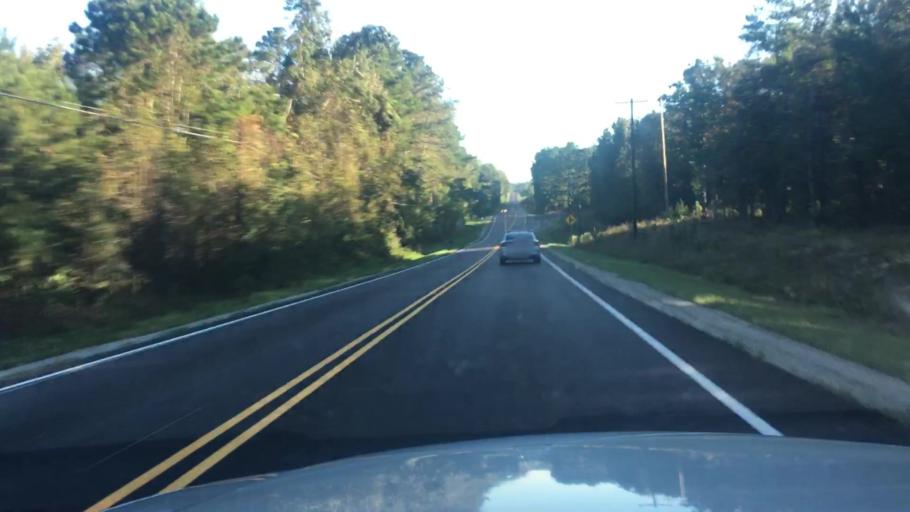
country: US
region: North Carolina
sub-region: Harnett County
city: Walkertown
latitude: 35.3386
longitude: -78.8573
